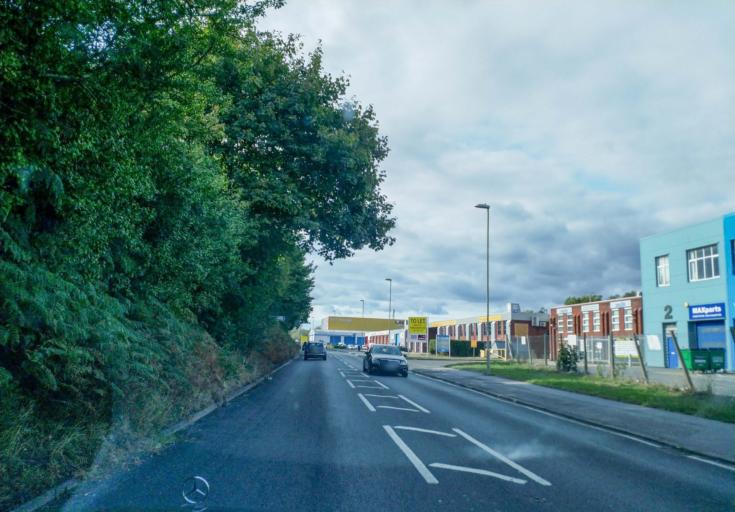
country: GB
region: England
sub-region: Surrey
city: Frimley
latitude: 51.3125
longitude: -0.7566
